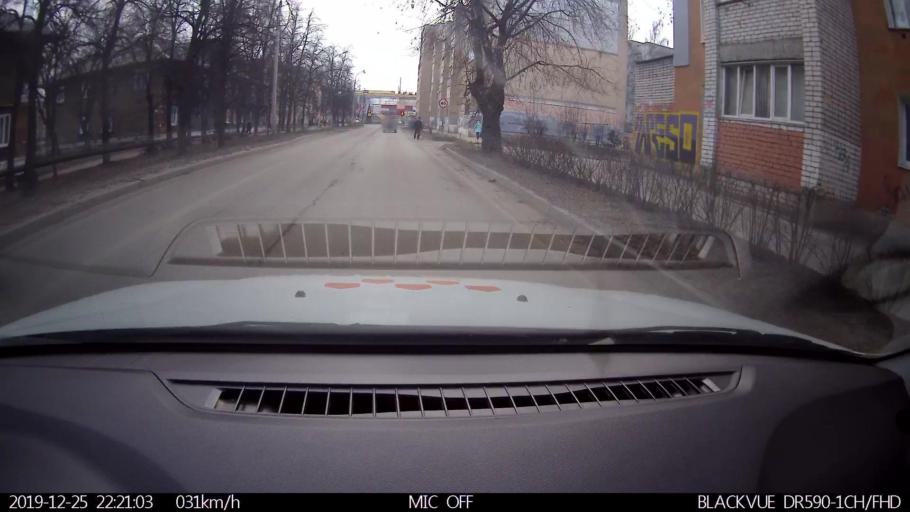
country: RU
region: Nizjnij Novgorod
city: Gorbatovka
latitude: 56.3329
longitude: 43.8399
